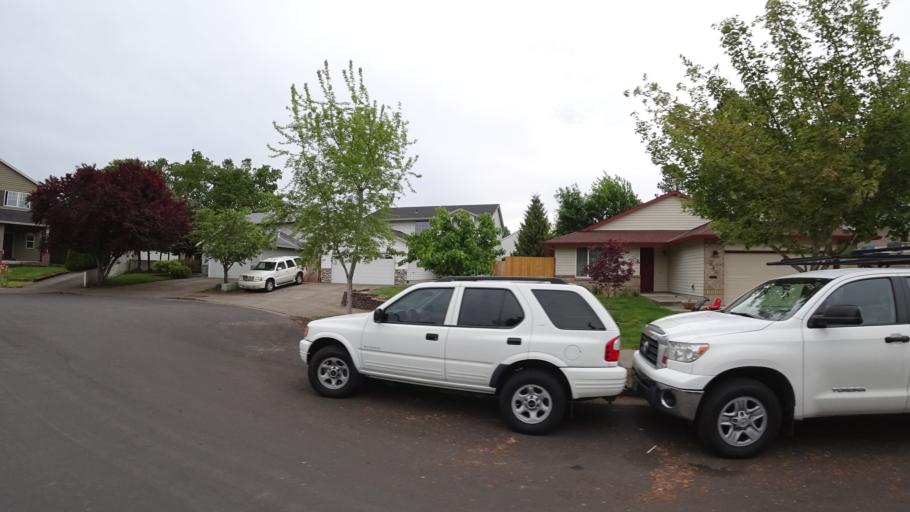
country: US
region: Oregon
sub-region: Washington County
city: Aloha
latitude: 45.5149
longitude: -122.9115
